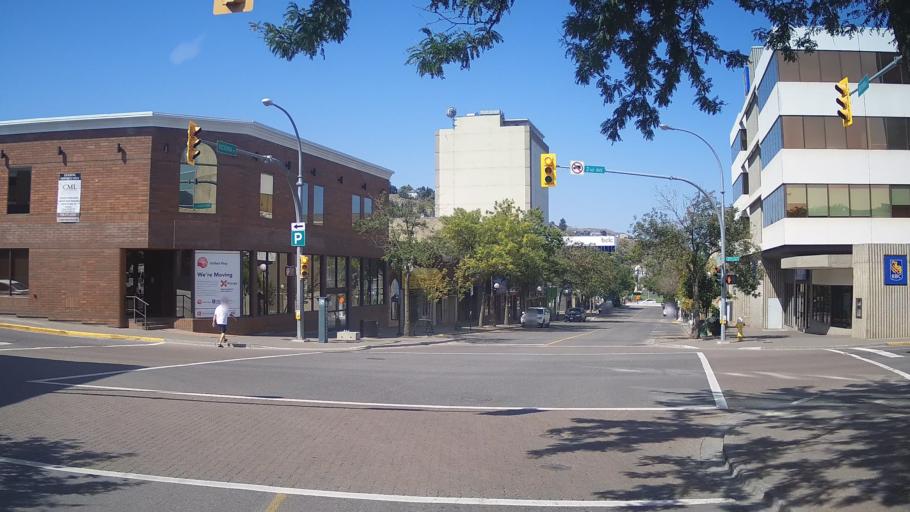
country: CA
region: British Columbia
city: Kamloops
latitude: 50.6758
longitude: -120.3362
